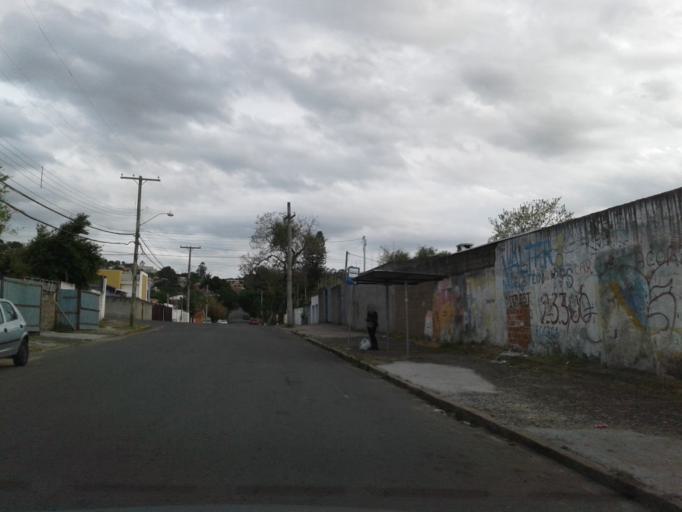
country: BR
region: Rio Grande do Sul
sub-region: Porto Alegre
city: Porto Alegre
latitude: -30.0556
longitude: -51.1466
